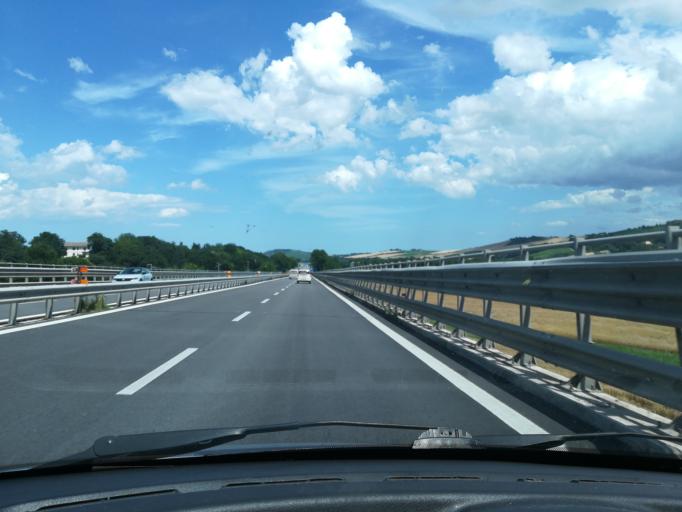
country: IT
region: The Marches
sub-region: Provincia di Macerata
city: Pollenza
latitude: 43.2323
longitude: 13.3569
